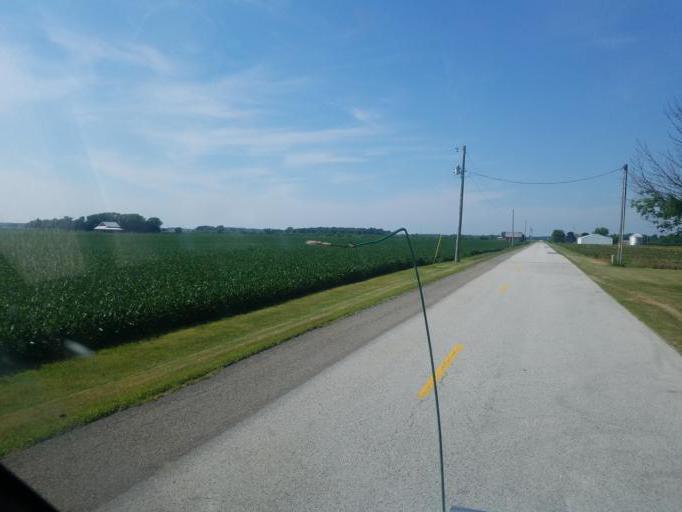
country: US
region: Ohio
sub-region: Logan County
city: Lakeview
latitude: 40.5445
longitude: -84.0120
